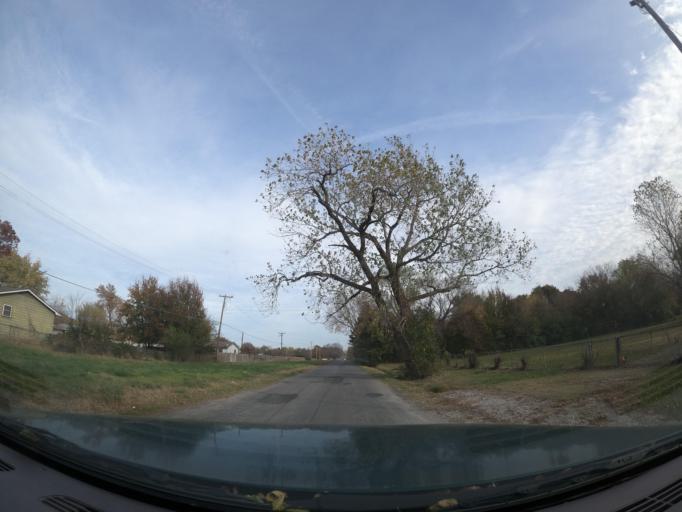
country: US
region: Oklahoma
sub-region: Tulsa County
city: Turley
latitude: 36.2422
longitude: -95.9963
